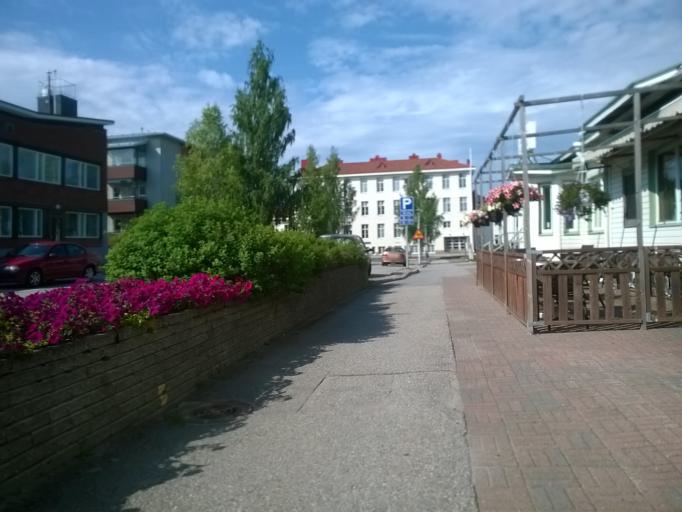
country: FI
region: Kainuu
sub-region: Kehys-Kainuu
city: Kuhmo
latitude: 64.1289
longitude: 29.5200
